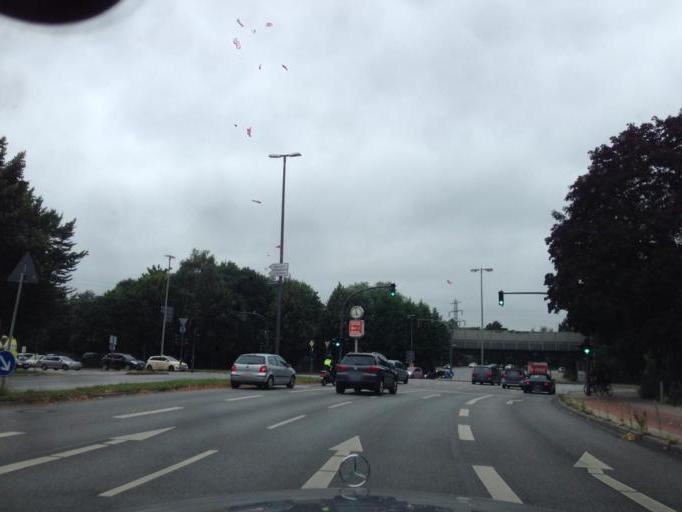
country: DE
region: Hamburg
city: Hamburg-Nord
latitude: 53.6004
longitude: 9.9840
